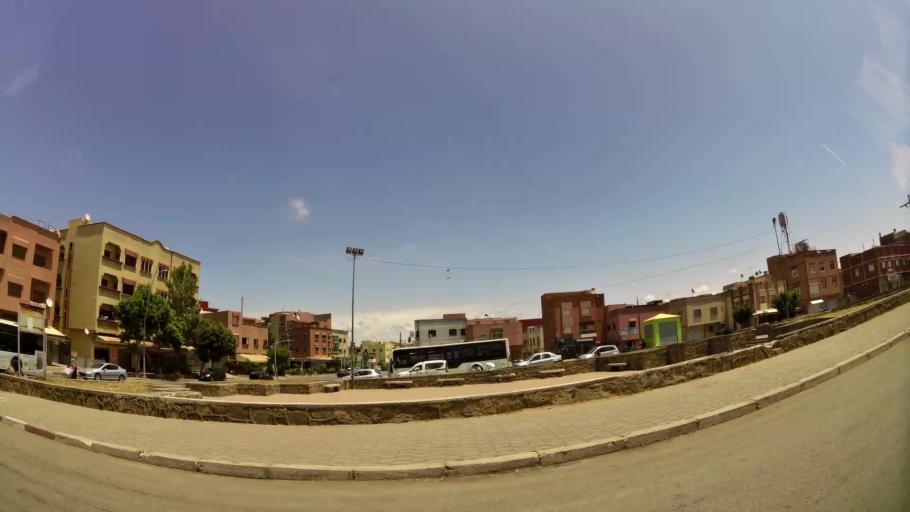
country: MA
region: Gharb-Chrarda-Beni Hssen
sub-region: Kenitra Province
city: Kenitra
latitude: 34.2656
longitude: -6.6176
